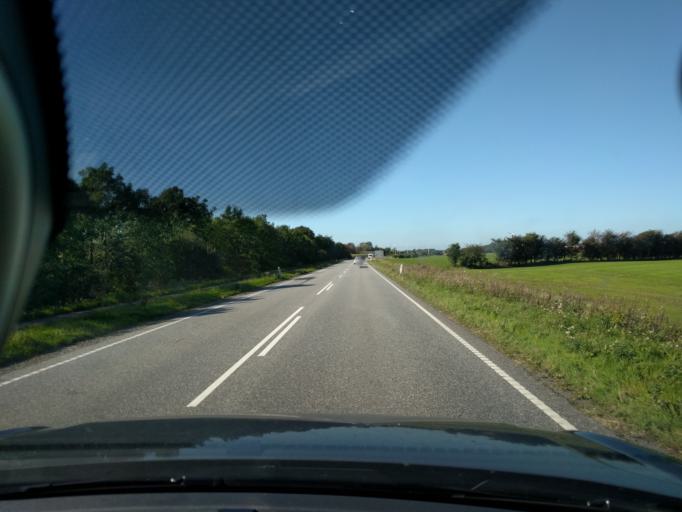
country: DK
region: North Denmark
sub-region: Mariagerfjord Kommune
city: Hobro
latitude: 56.6782
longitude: 9.6673
